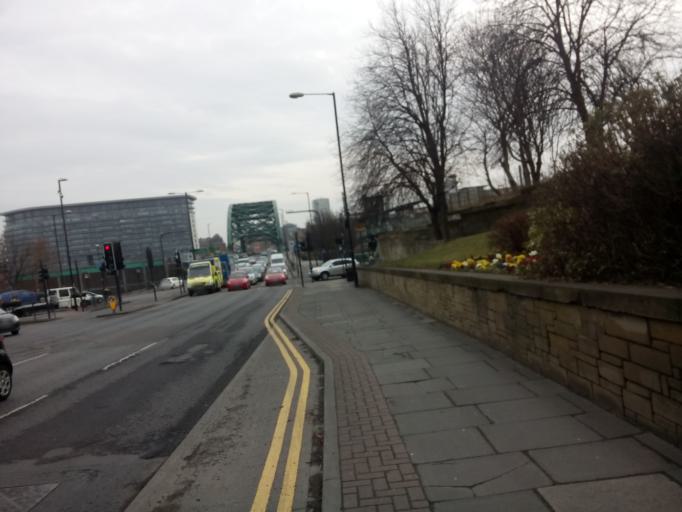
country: GB
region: England
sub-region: Sunderland
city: Sunderland
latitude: 54.9119
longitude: -1.3834
